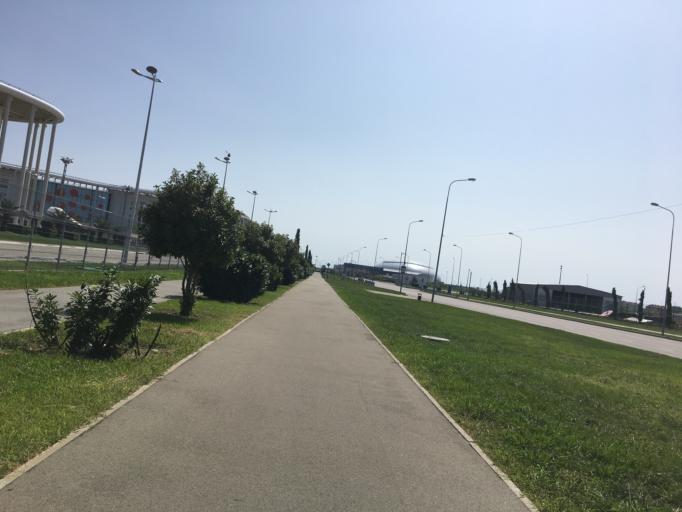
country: RU
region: Krasnodarskiy
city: Adler
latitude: 43.4155
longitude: 39.9477
